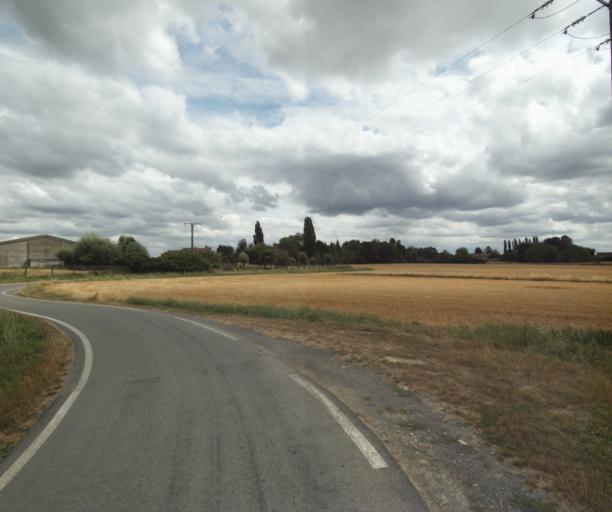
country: FR
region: Nord-Pas-de-Calais
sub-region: Departement du Nord
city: Linselles
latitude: 50.7502
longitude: 3.0736
